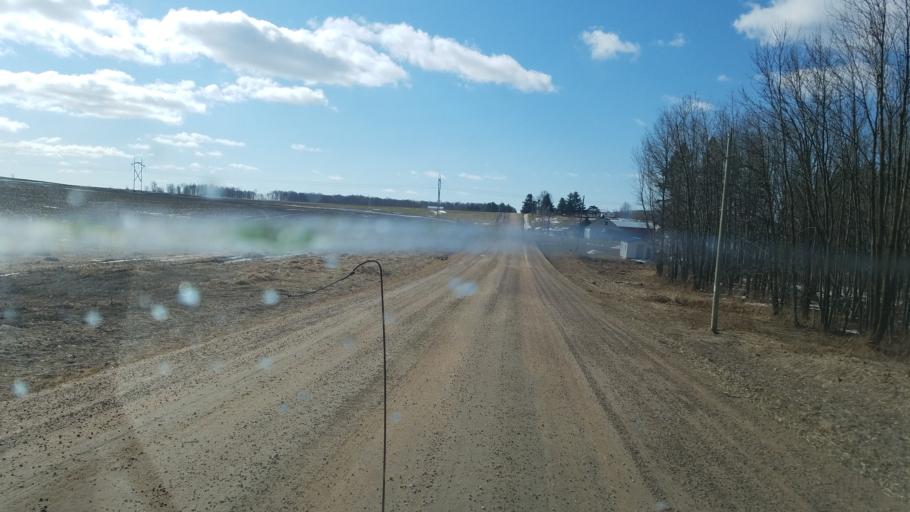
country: US
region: Wisconsin
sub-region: Clark County
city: Loyal
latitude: 44.6727
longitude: -90.4559
